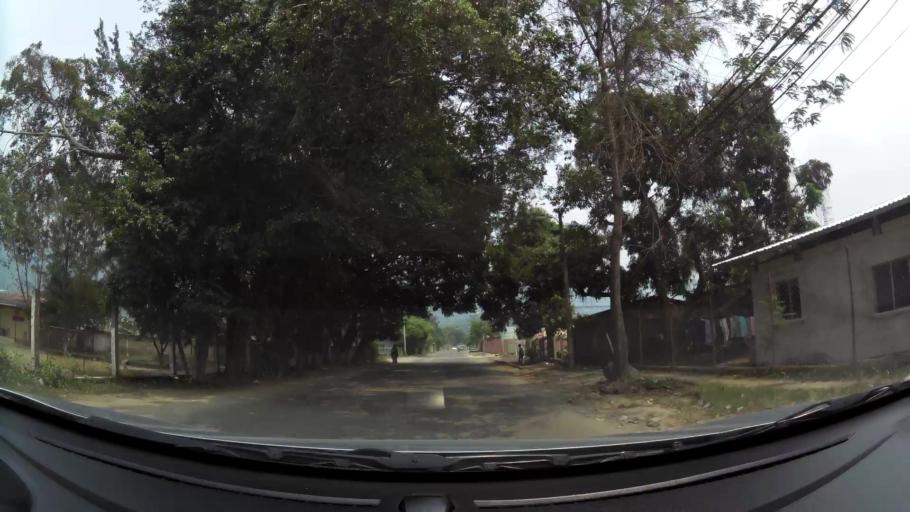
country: HN
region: Yoro
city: El Progreso
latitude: 15.3964
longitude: -87.7978
